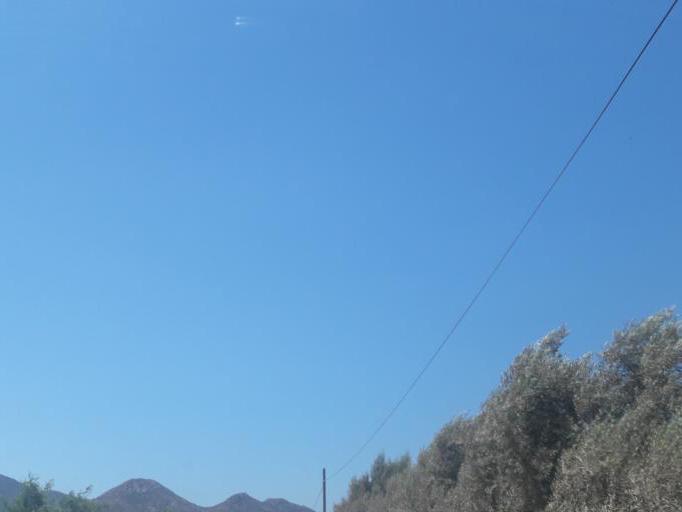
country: MX
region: Baja California
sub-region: Ensenada
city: Rancho Verde
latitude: 32.0850
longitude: -116.6251
